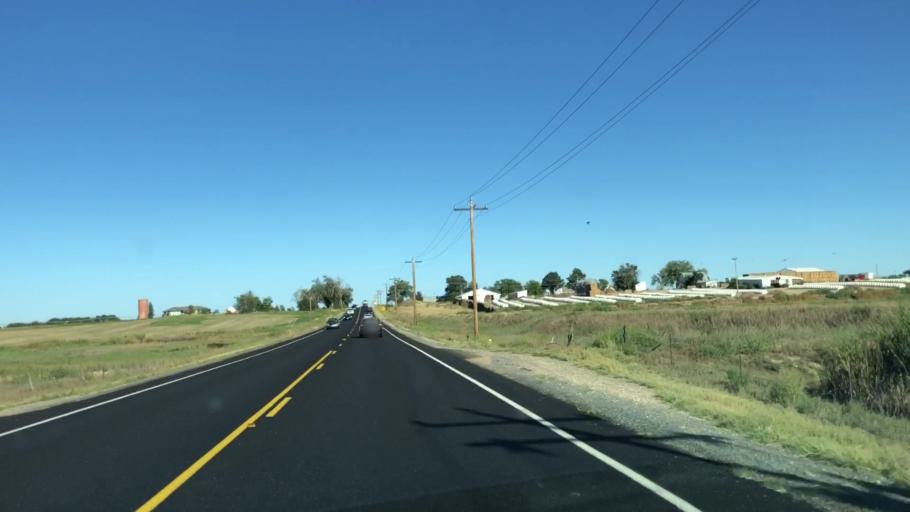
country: US
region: Colorado
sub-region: Larimer County
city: Loveland
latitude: 40.4656
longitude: -105.0304
